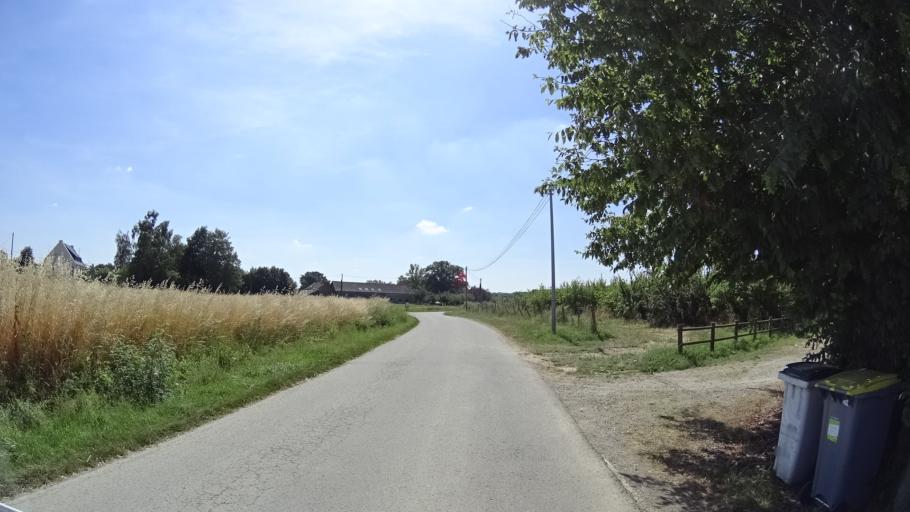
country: FR
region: Brittany
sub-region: Departement d'Ille-et-Vilaine
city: Orgeres
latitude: 48.0026
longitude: -1.6642
